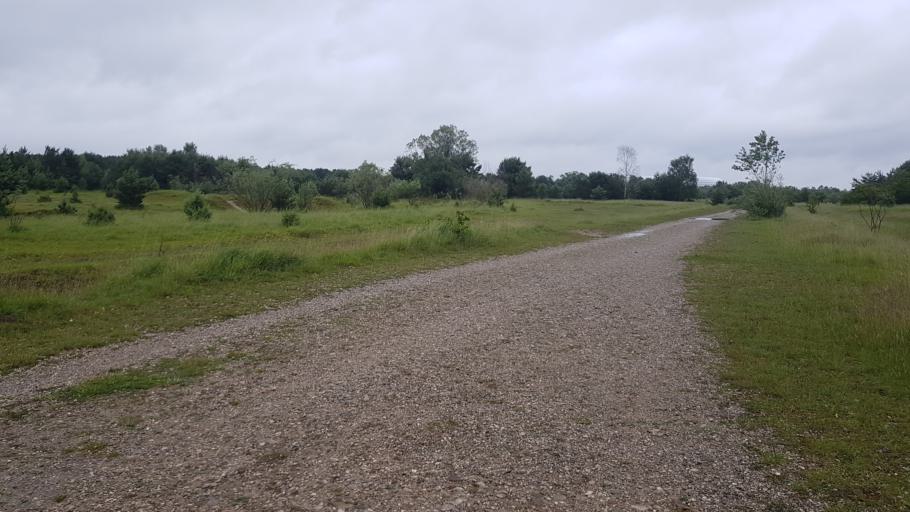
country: DE
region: Bavaria
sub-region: Upper Bavaria
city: Unterfoehring
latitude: 48.2103
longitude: 11.6051
